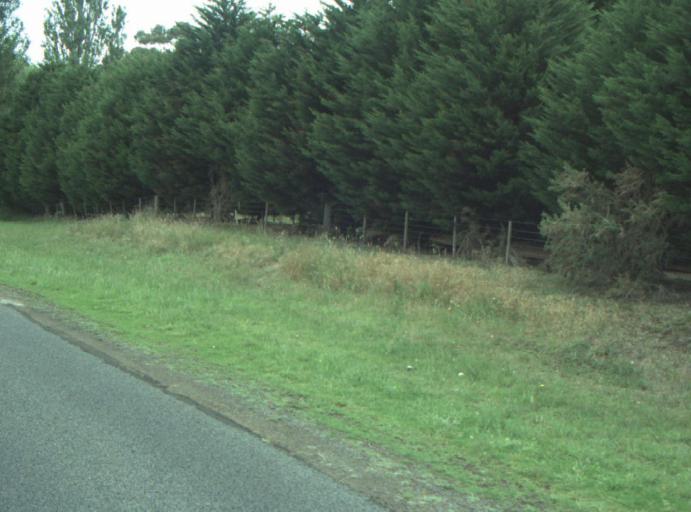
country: AU
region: Victoria
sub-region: Greater Geelong
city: Leopold
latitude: -38.2051
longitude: 144.5085
